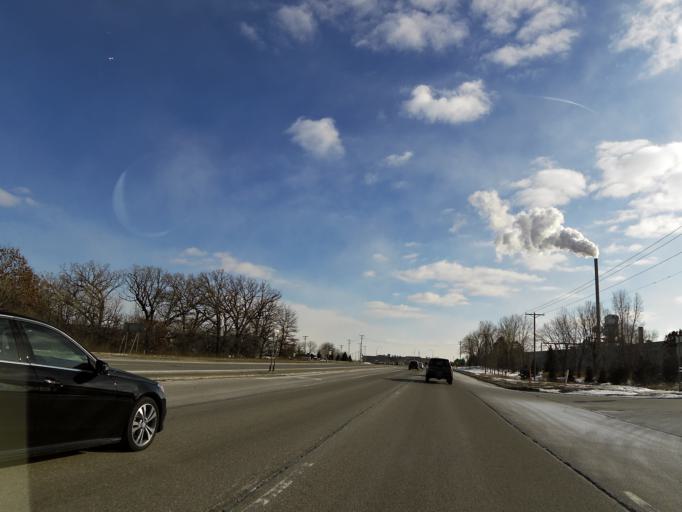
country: US
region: Minnesota
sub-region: Dakota County
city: Mendota Heights
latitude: 44.8372
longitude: -93.1180
